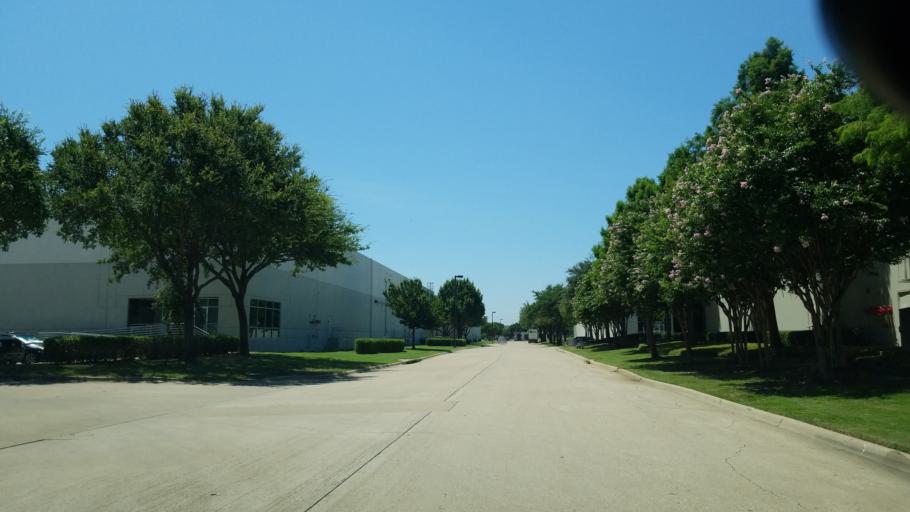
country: US
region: Texas
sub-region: Dallas County
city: Farmers Branch
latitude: 32.9439
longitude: -96.9270
